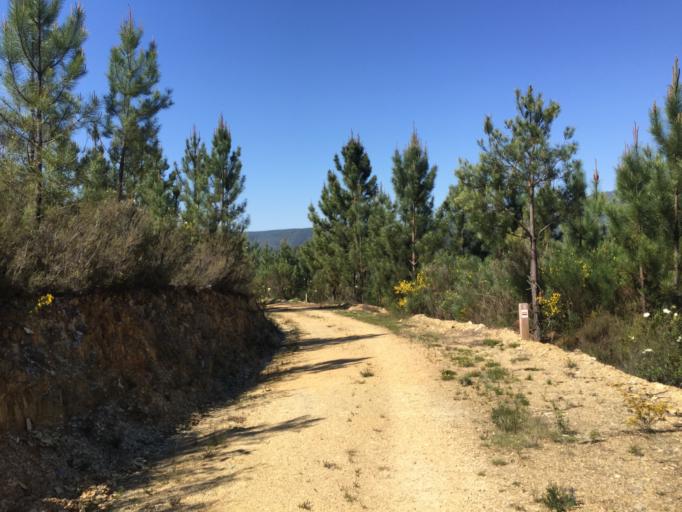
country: PT
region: Coimbra
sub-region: Pampilhosa da Serra
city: Pampilhosa da Serra
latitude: 40.0853
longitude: -7.7809
